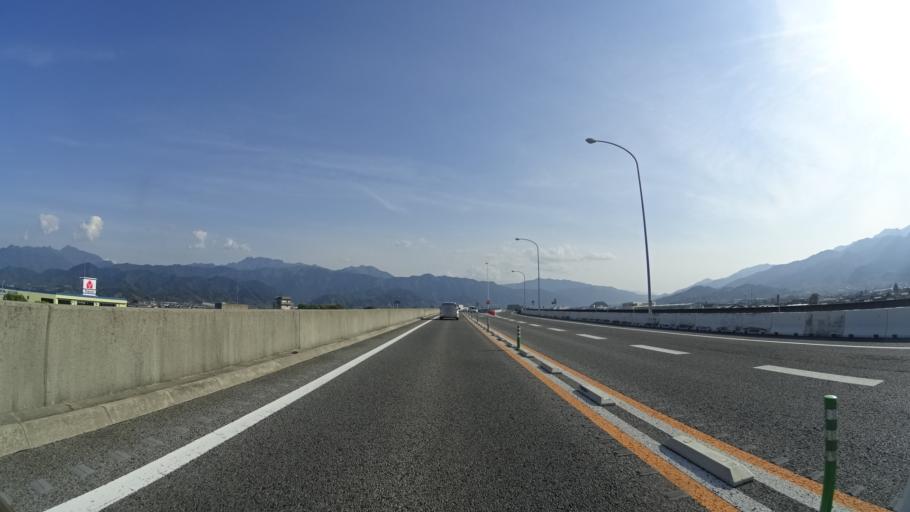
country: JP
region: Ehime
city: Saijo
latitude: 33.9196
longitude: 133.0742
